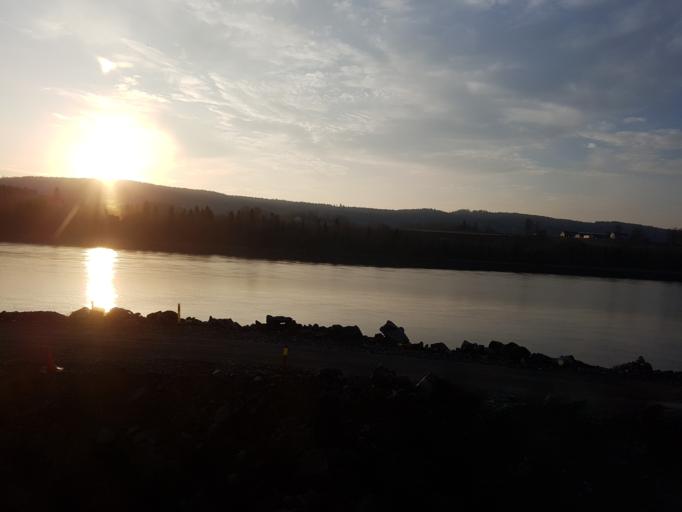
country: NO
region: Akershus
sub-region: Eidsvoll
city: Eidsvoll
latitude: 60.3557
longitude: 11.2454
